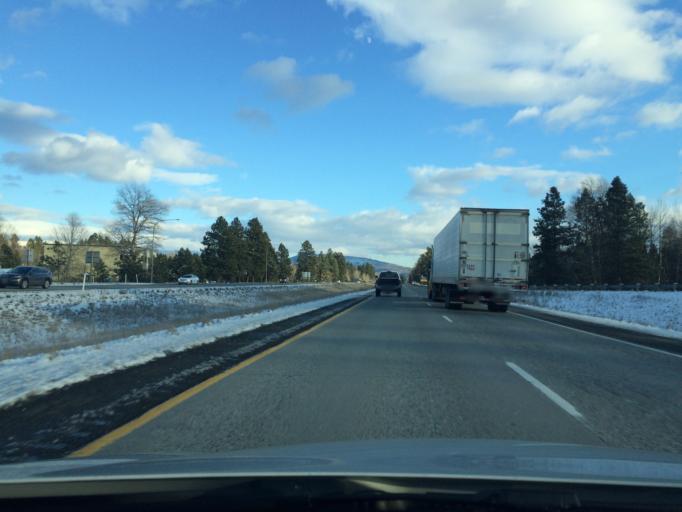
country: US
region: Washington
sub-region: Kittitas County
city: Cle Elum
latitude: 47.1909
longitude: -120.9350
